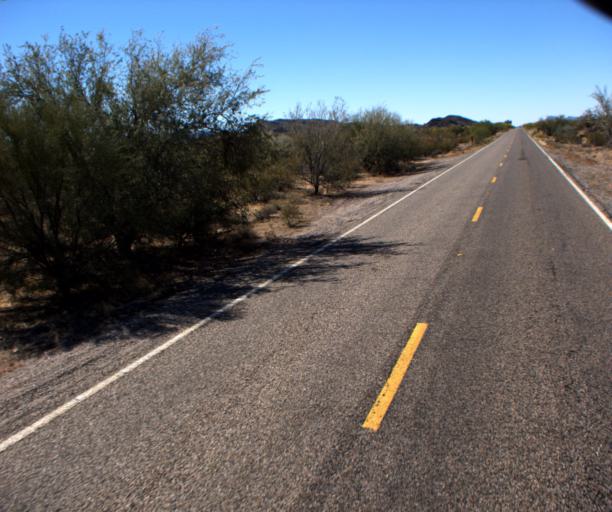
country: US
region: Arizona
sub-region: Pima County
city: Ajo
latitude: 32.2458
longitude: -112.7476
